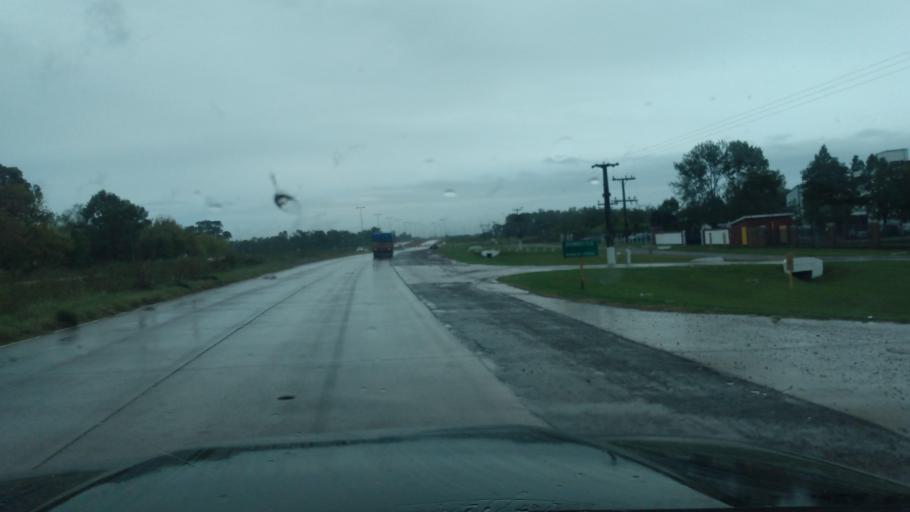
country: AR
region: Buenos Aires
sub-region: Partido de Pilar
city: Pilar
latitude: -34.3909
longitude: -59.0191
